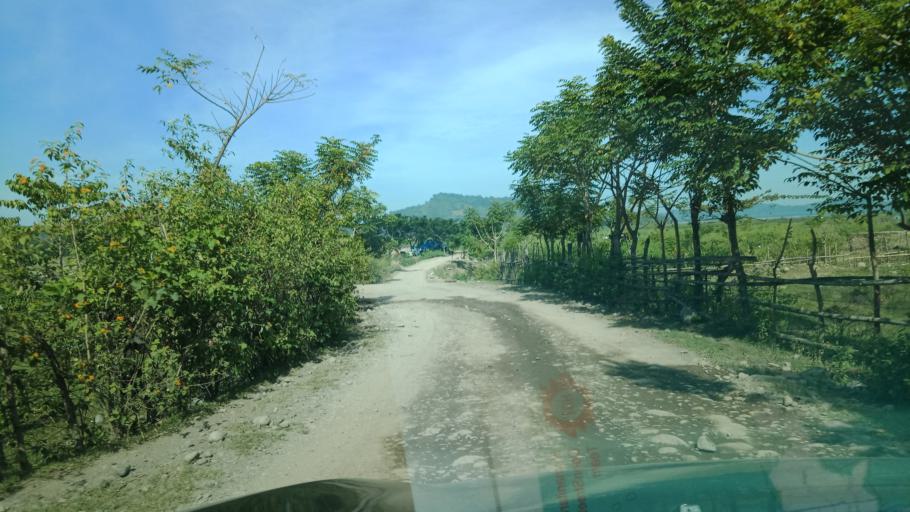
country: ID
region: South Sulawesi
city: Makassar
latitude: -5.2558
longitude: 119.6427
